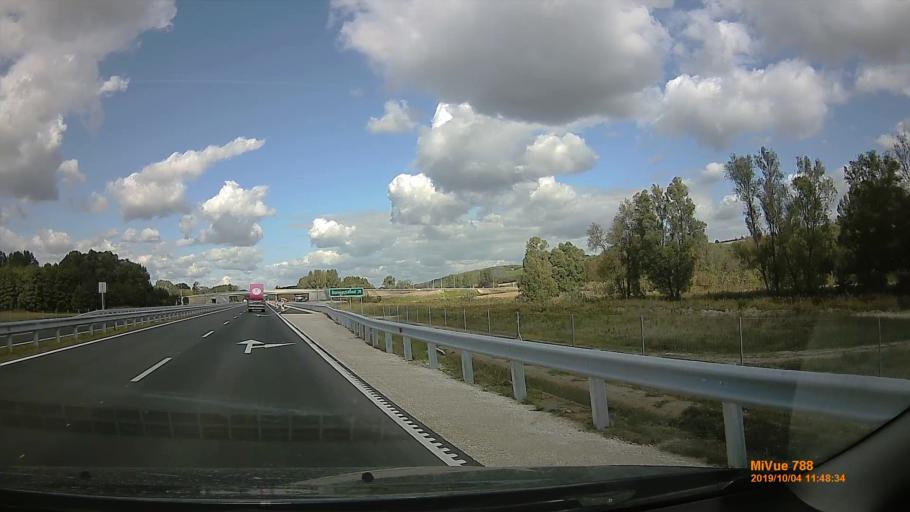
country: HU
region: Somogy
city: Karad
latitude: 46.6636
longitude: 17.7841
